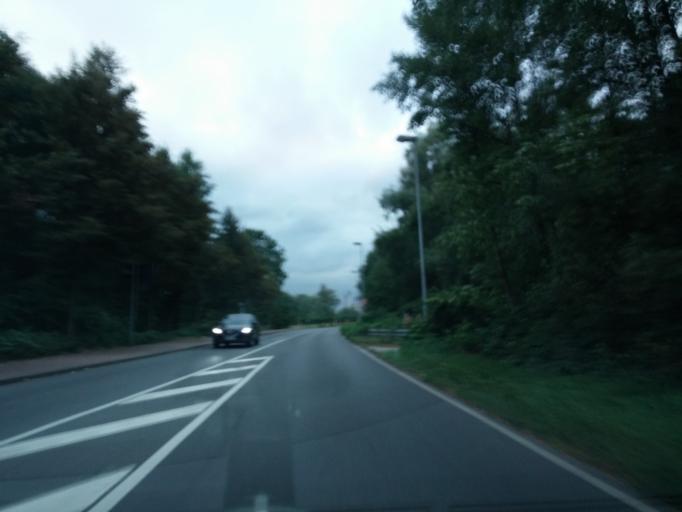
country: DE
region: North Rhine-Westphalia
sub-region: Regierungsbezirk Munster
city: Gladbeck
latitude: 51.5662
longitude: 7.0284
